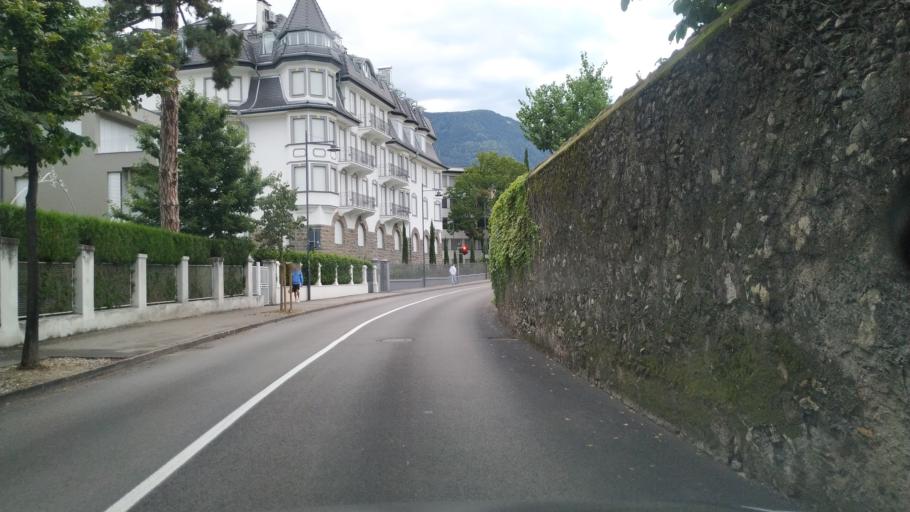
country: IT
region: Trentino-Alto Adige
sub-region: Bolzano
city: Merano
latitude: 46.6746
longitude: 11.1580
